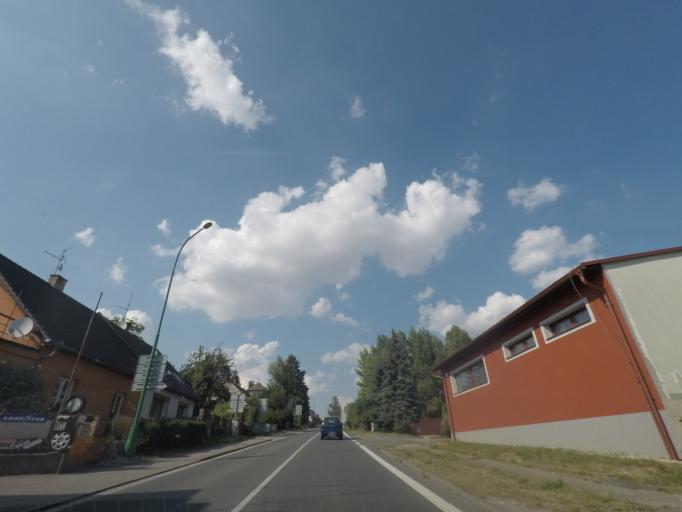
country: CZ
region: Kralovehradecky
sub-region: Okres Nachod
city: Jaromer
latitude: 50.3571
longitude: 15.9049
